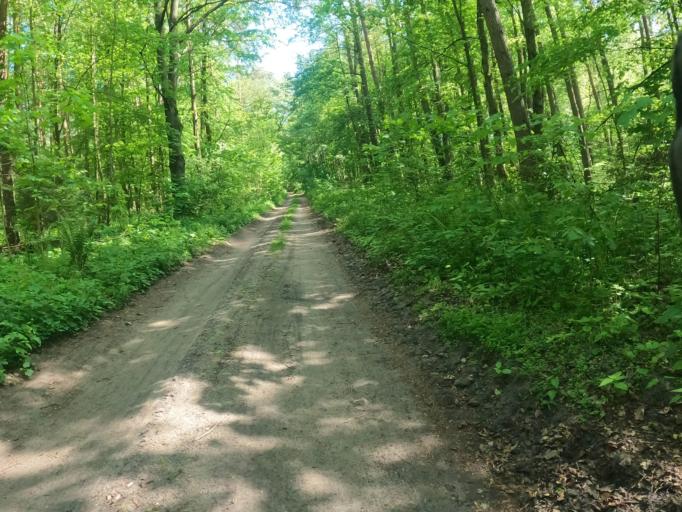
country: PL
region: West Pomeranian Voivodeship
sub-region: Powiat mysliborski
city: Barlinek
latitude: 53.0209
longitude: 15.2386
